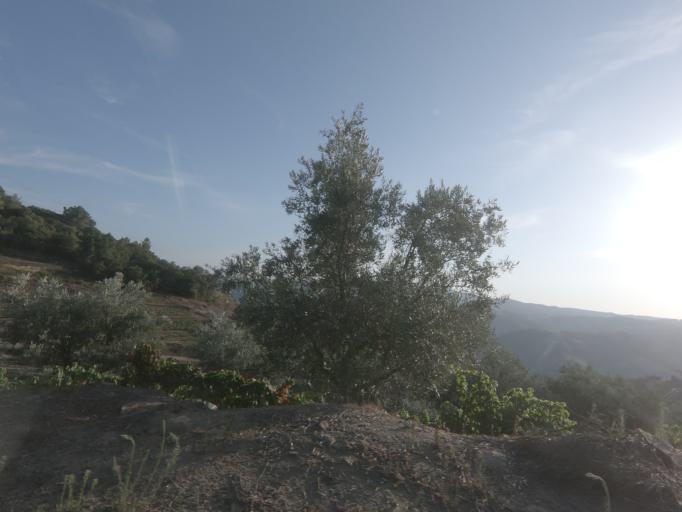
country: PT
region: Vila Real
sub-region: Sabrosa
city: Sabrosa
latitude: 41.2662
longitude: -7.5322
